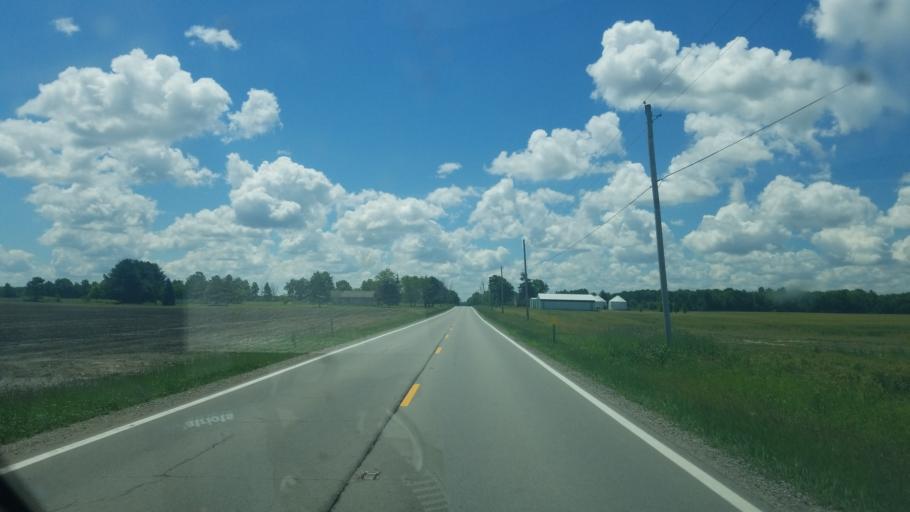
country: US
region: Ohio
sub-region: Huron County
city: New London
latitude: 41.1577
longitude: -82.4102
